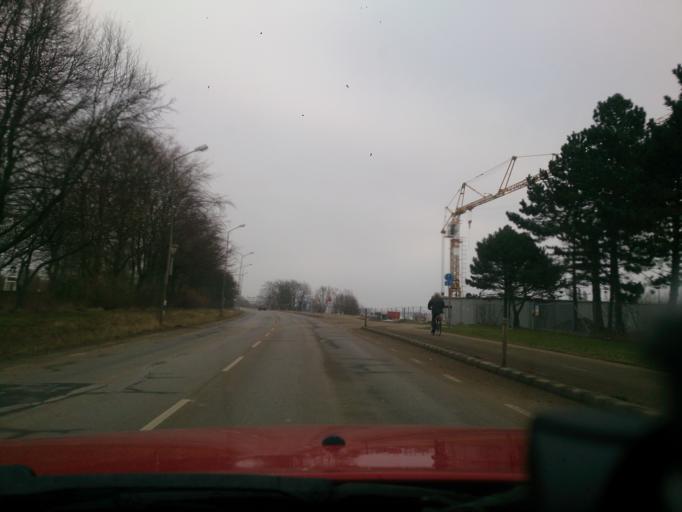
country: SE
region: Skane
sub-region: Ystads Kommun
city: Ystad
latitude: 55.4248
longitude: 13.7911
